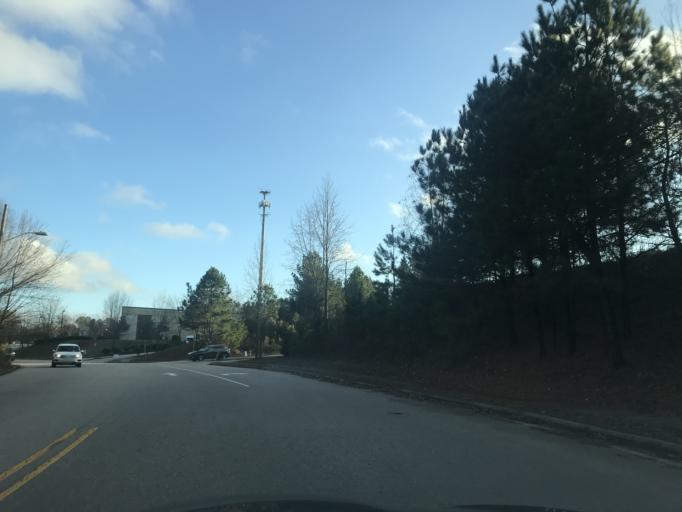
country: US
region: North Carolina
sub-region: Wake County
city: Wake Forest
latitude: 35.9529
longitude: -78.5336
